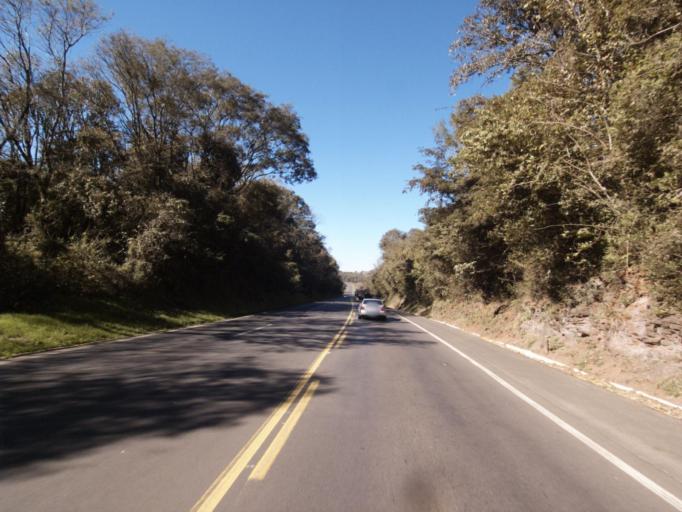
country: BR
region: Santa Catarina
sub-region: Chapeco
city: Chapeco
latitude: -26.9957
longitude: -52.6239
